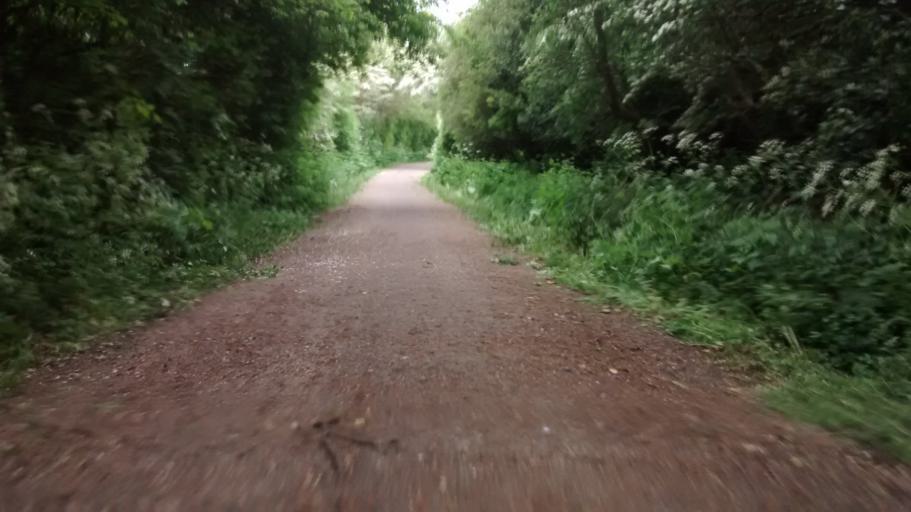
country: GB
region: England
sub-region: County Durham
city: West Rainton
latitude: 54.7805
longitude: -1.5236
